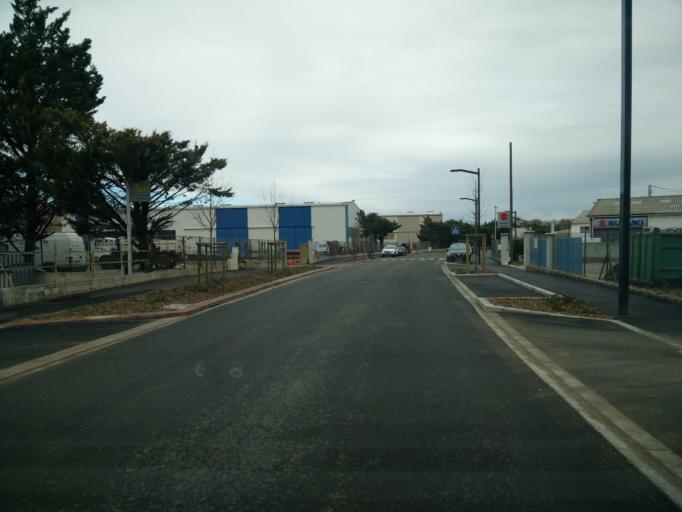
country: FR
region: Provence-Alpes-Cote d'Azur
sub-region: Departement du Var
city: Brignoles
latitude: 43.4003
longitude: 6.0502
